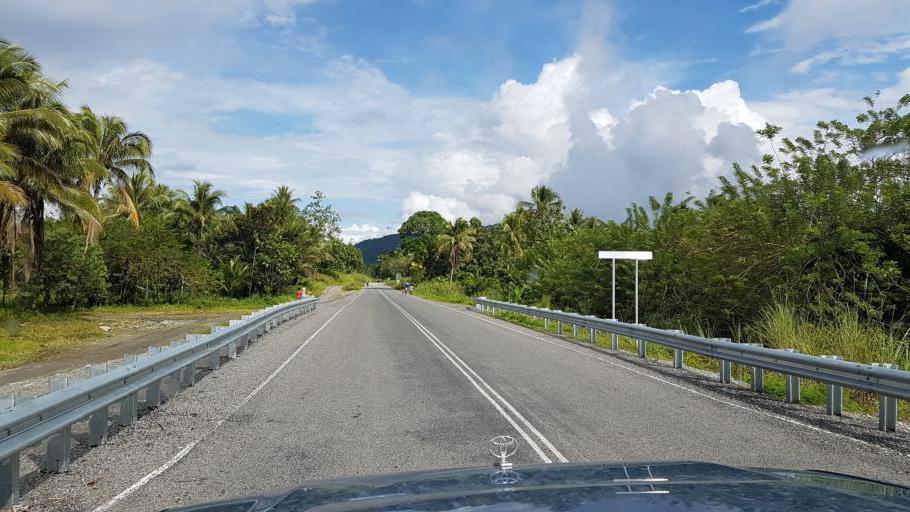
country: PG
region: Northern Province
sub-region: Sohe
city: Kokoda
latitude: -8.9053
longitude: 147.9797
